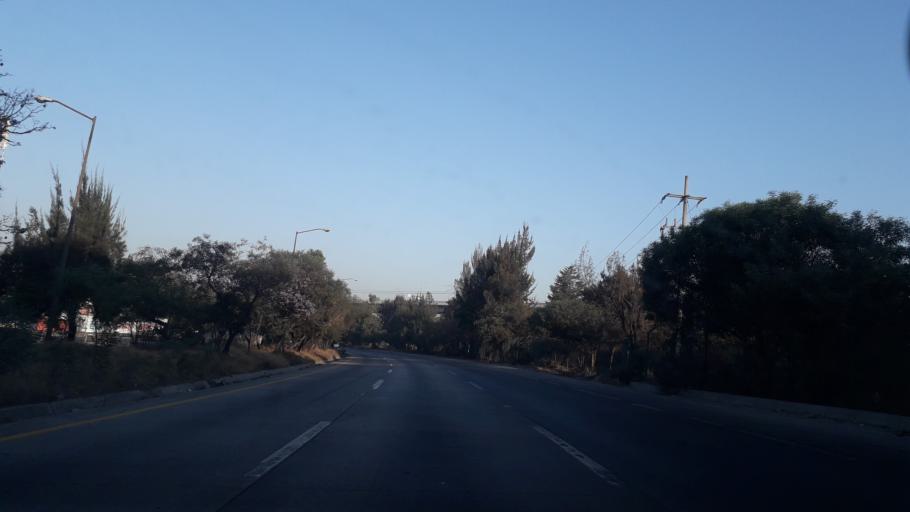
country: MX
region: Puebla
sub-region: Puebla
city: San Sebastian de Aparicio
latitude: 19.0810
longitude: -98.1656
